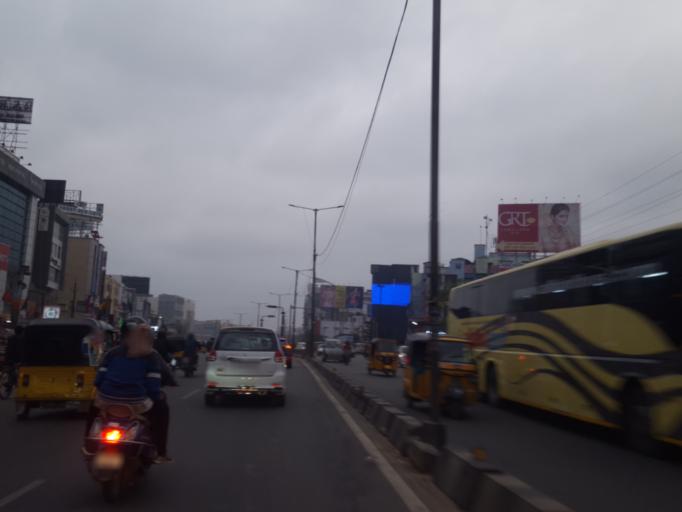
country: IN
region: Telangana
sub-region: Medak
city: Serilingampalle
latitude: 17.4951
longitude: 78.3310
